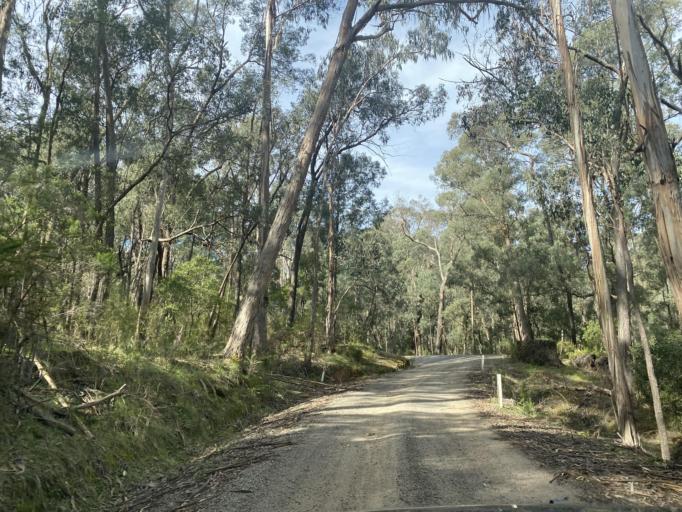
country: AU
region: Victoria
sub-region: Mansfield
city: Mansfield
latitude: -36.8239
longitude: 146.1479
